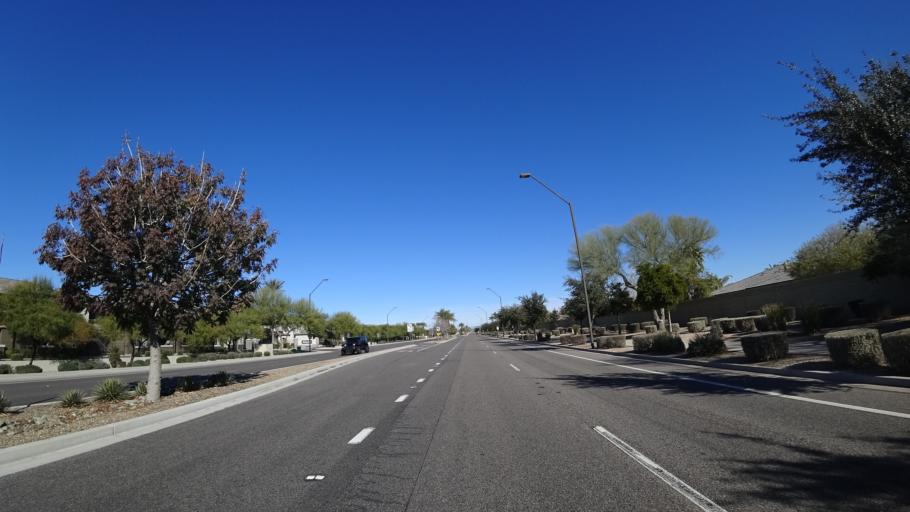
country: US
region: Arizona
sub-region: Maricopa County
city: Litchfield Park
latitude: 33.4727
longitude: -112.3753
